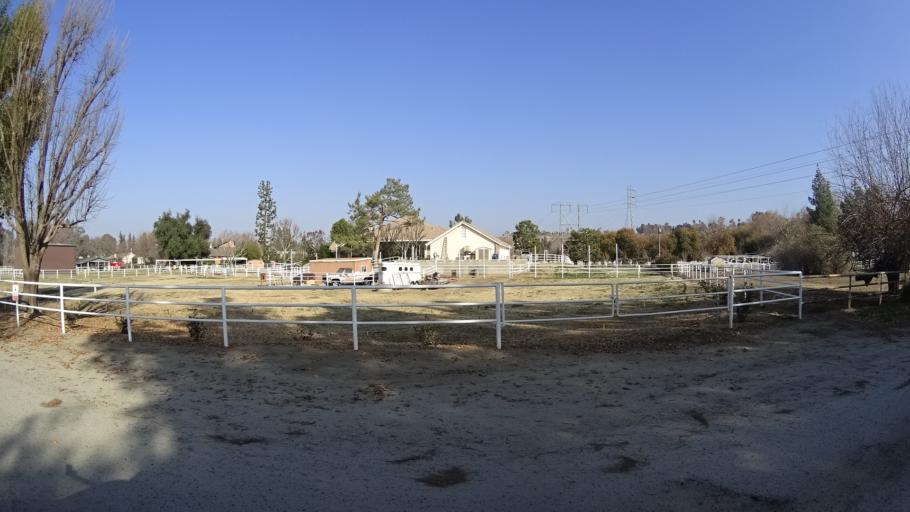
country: US
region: California
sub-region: Kern County
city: Oildale
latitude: 35.4062
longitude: -119.0048
